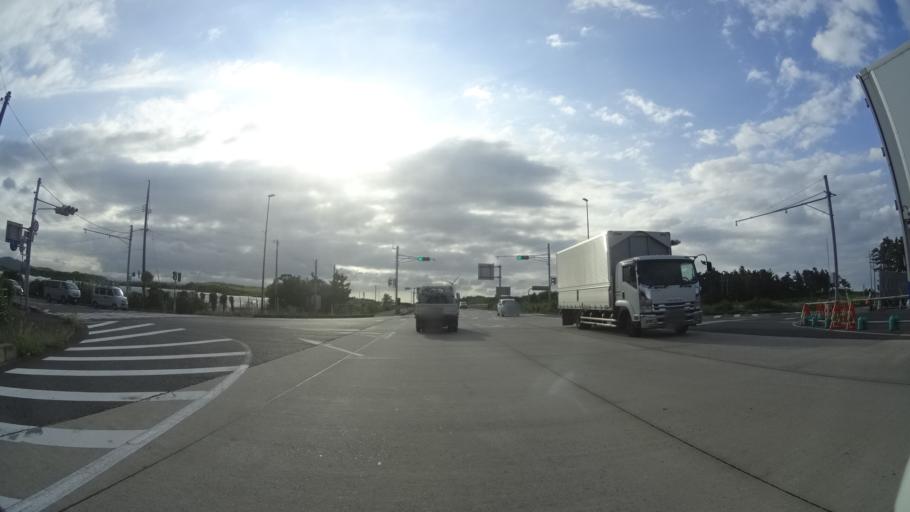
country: JP
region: Tottori
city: Kurayoshi
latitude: 35.4986
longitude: 133.8173
